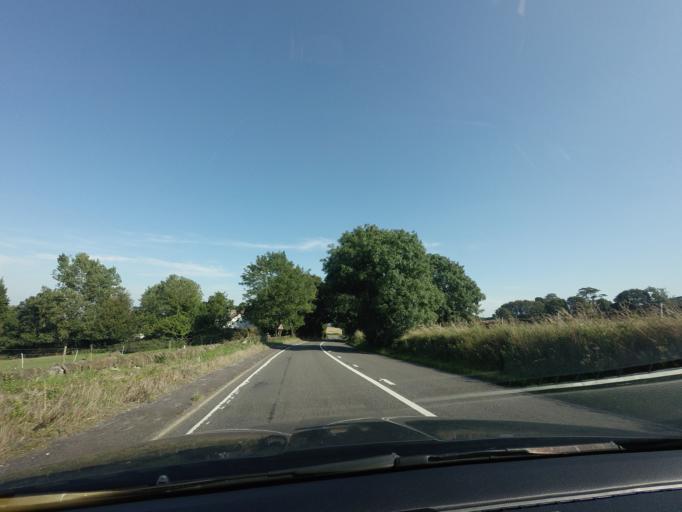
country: GB
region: England
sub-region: Derbyshire
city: Dronfield
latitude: 53.2325
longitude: -1.5267
